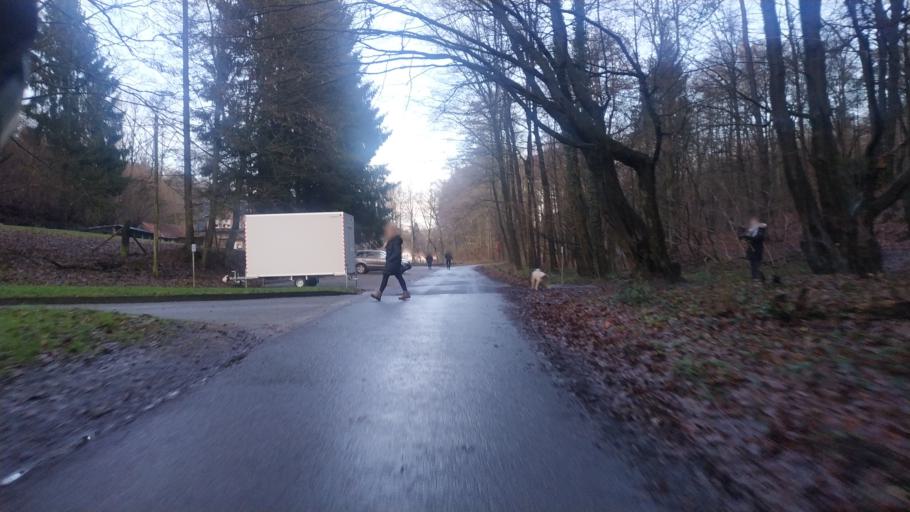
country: DE
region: North Rhine-Westphalia
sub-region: Regierungsbezirk Munster
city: Mettingen
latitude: 52.3079
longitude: 7.7724
